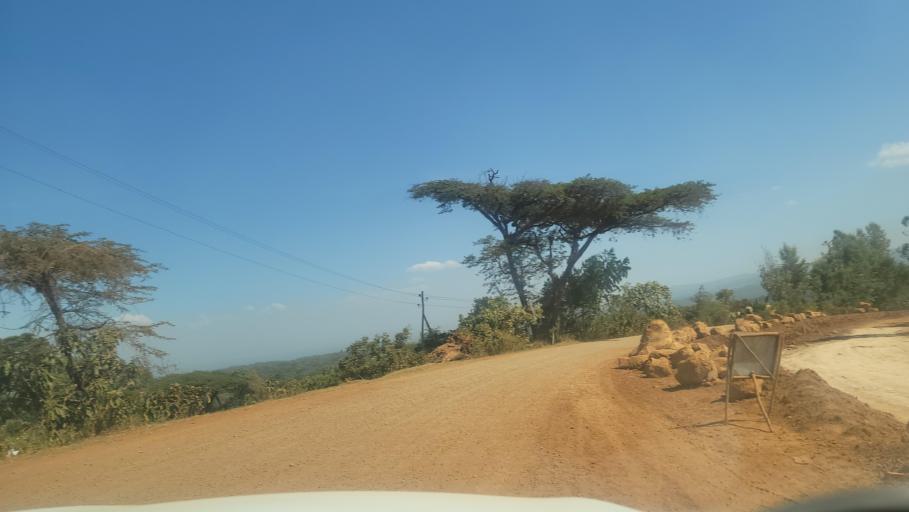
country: ET
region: Oromiya
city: Agaro
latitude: 7.8243
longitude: 36.5326
